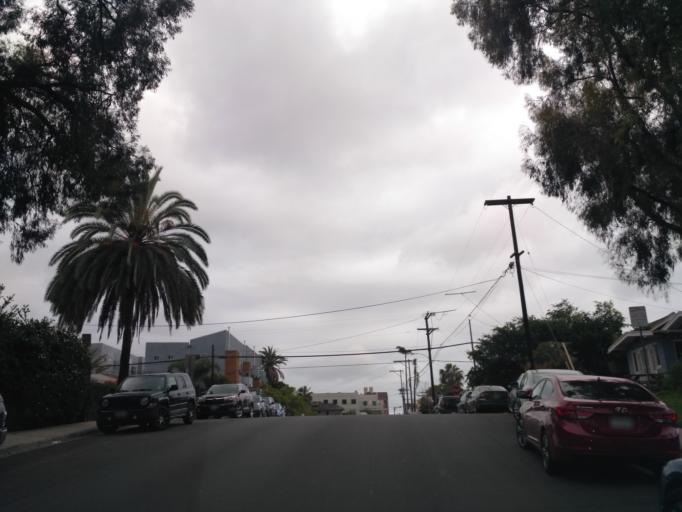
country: US
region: California
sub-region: San Diego County
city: San Diego
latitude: 32.7535
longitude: -117.1633
